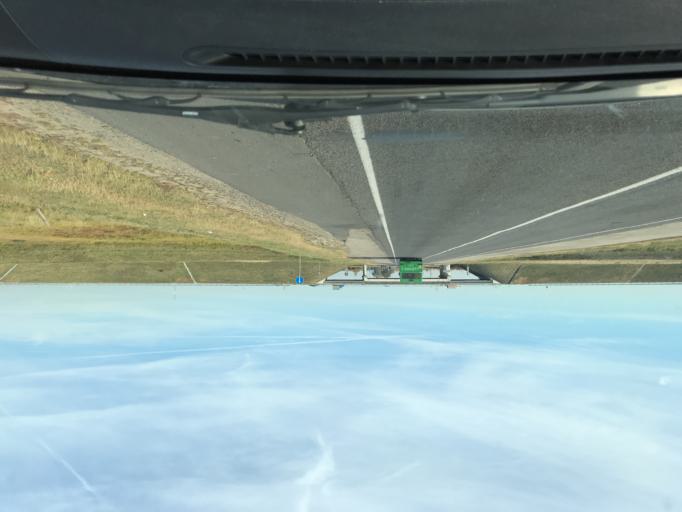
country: BY
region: Brest
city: Asnyezhytsy
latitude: 52.1826
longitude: 26.0822
